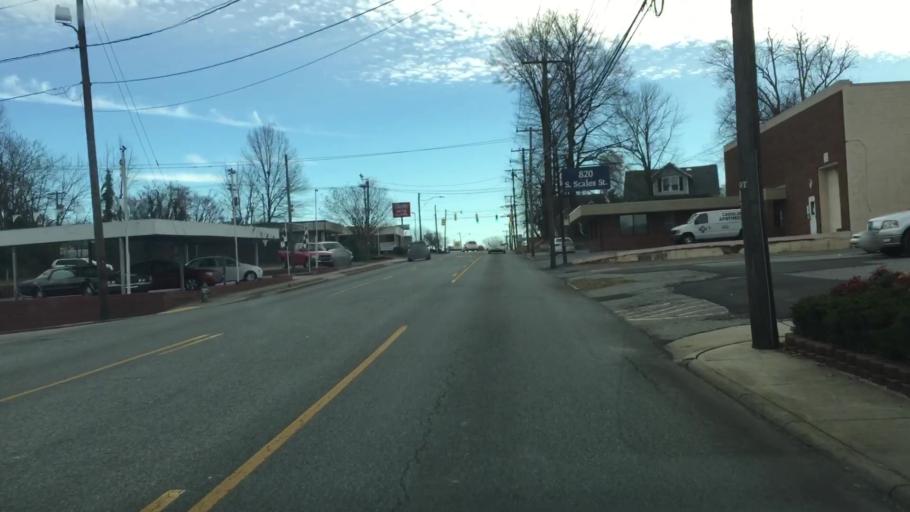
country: US
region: North Carolina
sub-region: Rockingham County
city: Reidsville
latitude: 36.3501
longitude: -79.6650
